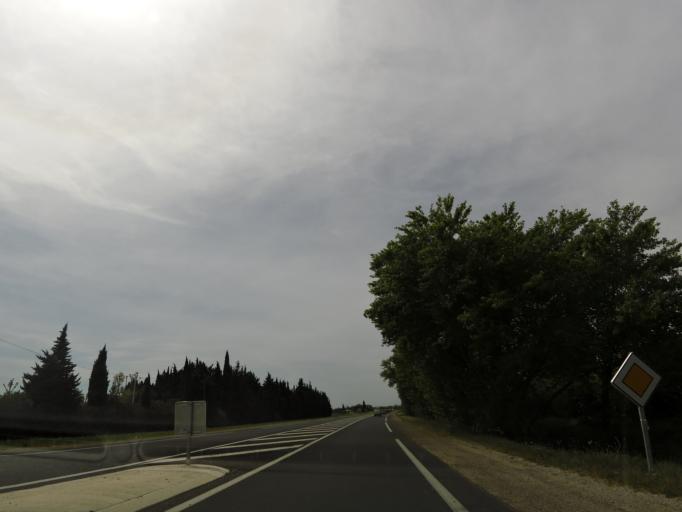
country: FR
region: Languedoc-Roussillon
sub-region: Departement de l'Herault
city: Lunel
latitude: 43.6709
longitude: 4.1458
